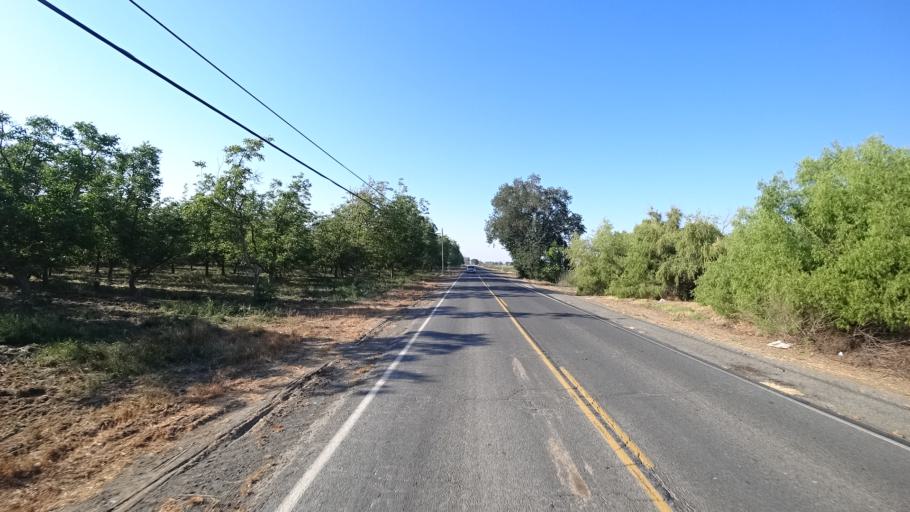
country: US
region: California
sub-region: Kings County
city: Armona
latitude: 36.2833
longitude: -119.7091
